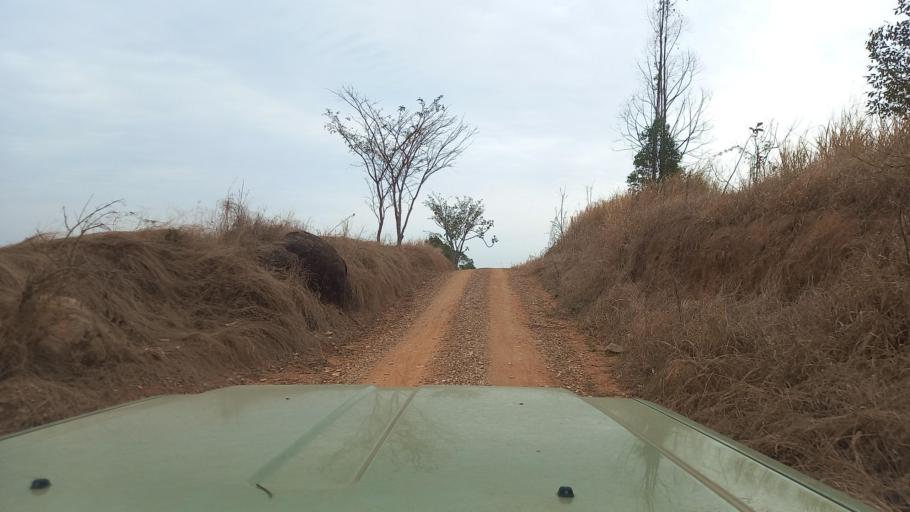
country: BR
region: Sao Paulo
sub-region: Moji-Guacu
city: Mogi-Gaucu
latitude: -22.2791
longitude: -46.8307
